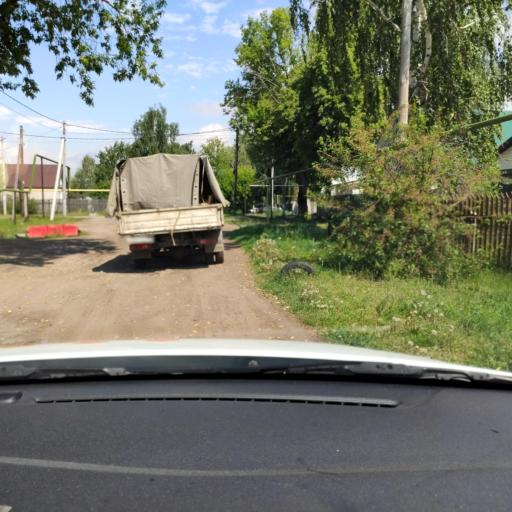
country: RU
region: Tatarstan
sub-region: Gorod Kazan'
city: Kazan
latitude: 55.7141
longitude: 49.0984
